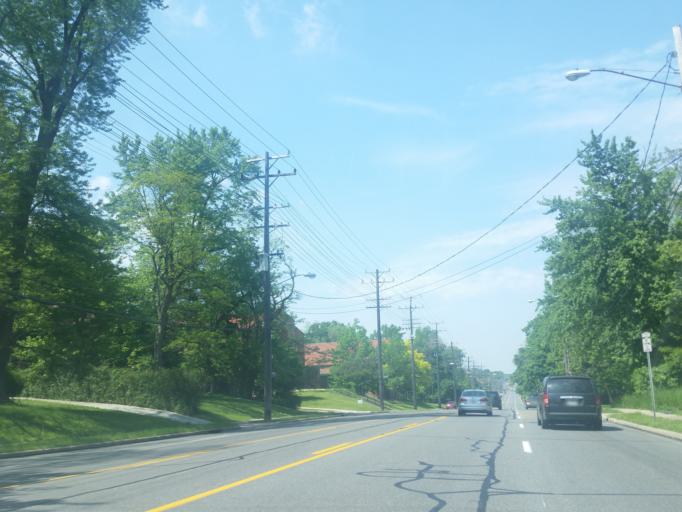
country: US
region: Ohio
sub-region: Cuyahoga County
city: Cleveland Heights
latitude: 41.5198
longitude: -81.5586
